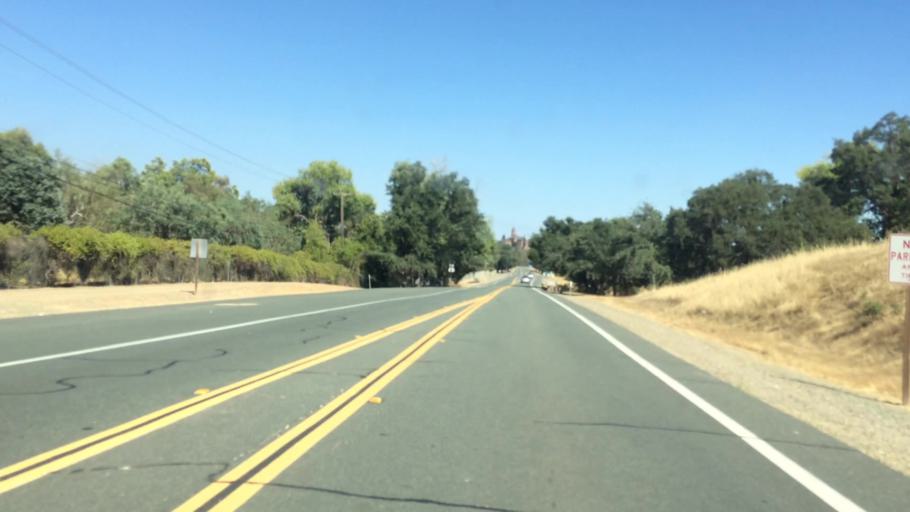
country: US
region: California
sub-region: Amador County
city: Ione
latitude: 38.3668
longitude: -120.9542
